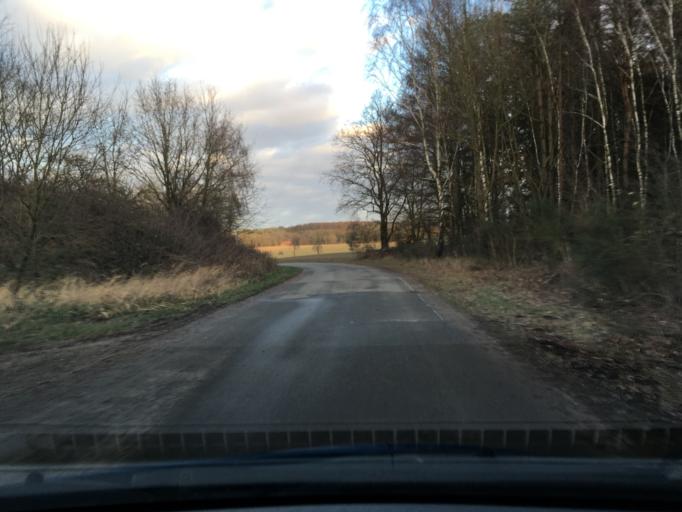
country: DE
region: Lower Saxony
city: Amelinghausen
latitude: 53.1360
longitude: 10.1860
